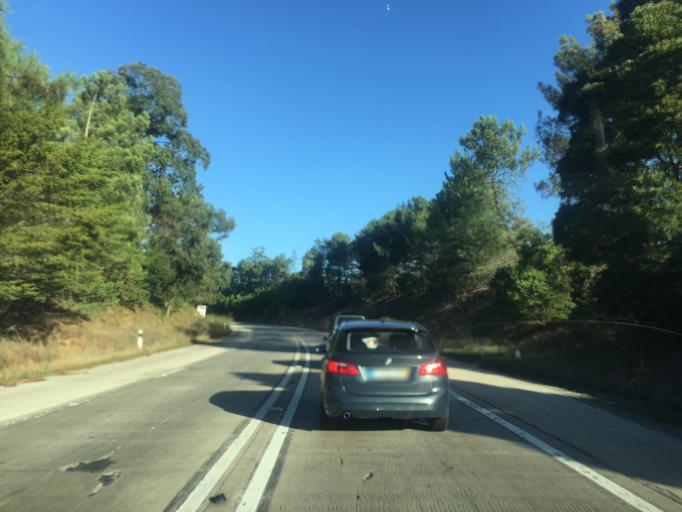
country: PT
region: Santarem
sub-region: Rio Maior
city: Rio Maior
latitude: 39.3163
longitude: -8.9364
